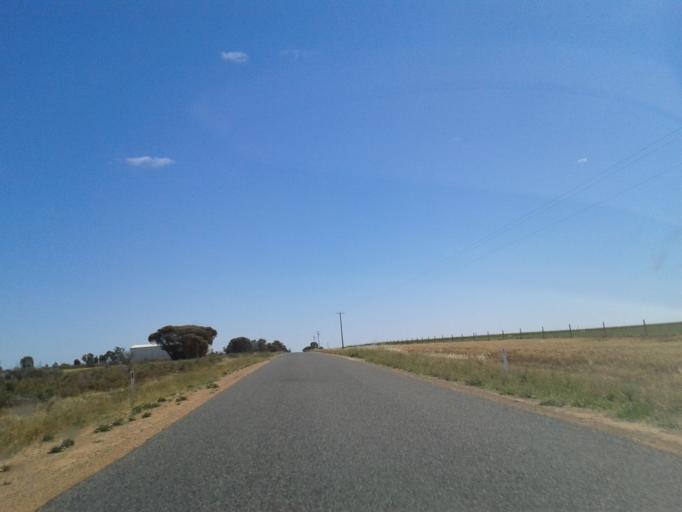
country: AU
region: New South Wales
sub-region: Wentworth
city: Dareton
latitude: -34.2118
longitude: 141.9970
